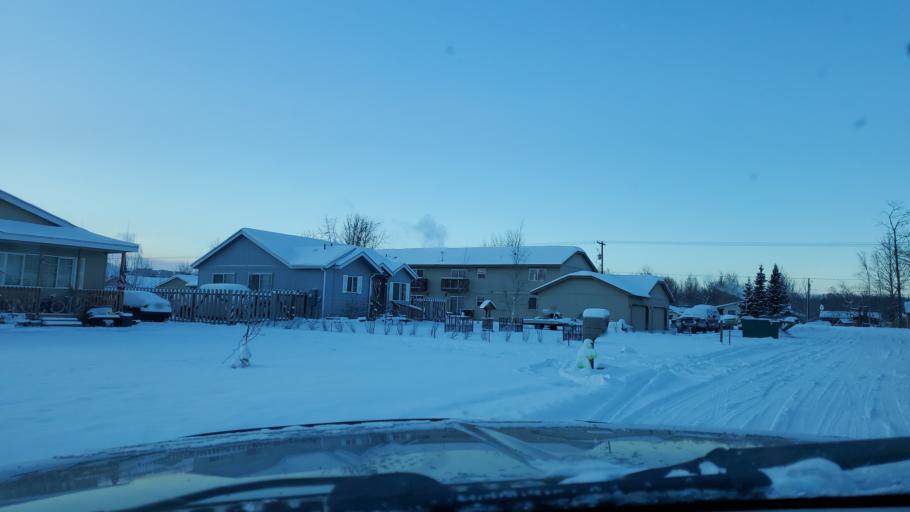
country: US
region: Alaska
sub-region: Matanuska-Susitna Borough
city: Palmer
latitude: 61.5907
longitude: -149.1087
